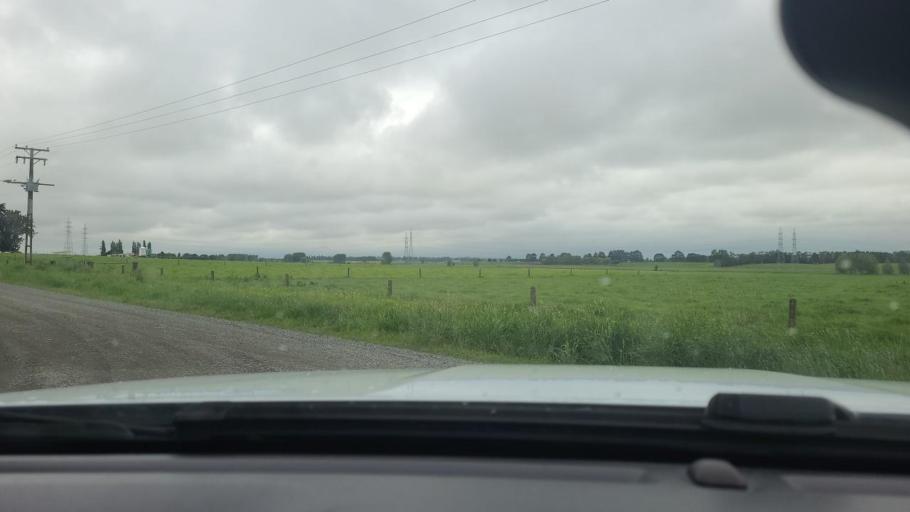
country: NZ
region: Southland
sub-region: Southland District
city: Riverton
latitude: -46.0658
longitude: 168.0536
